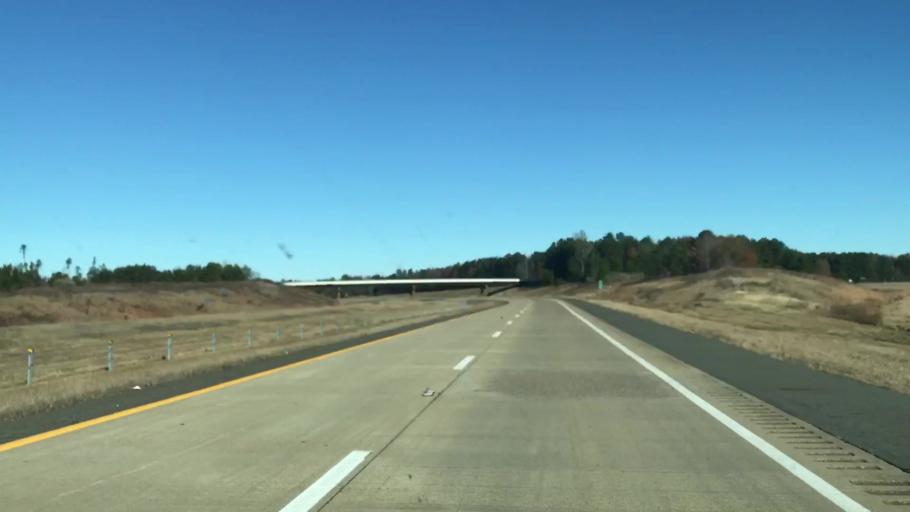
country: US
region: Texas
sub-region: Bowie County
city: Texarkana
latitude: 33.2660
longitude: -93.8975
